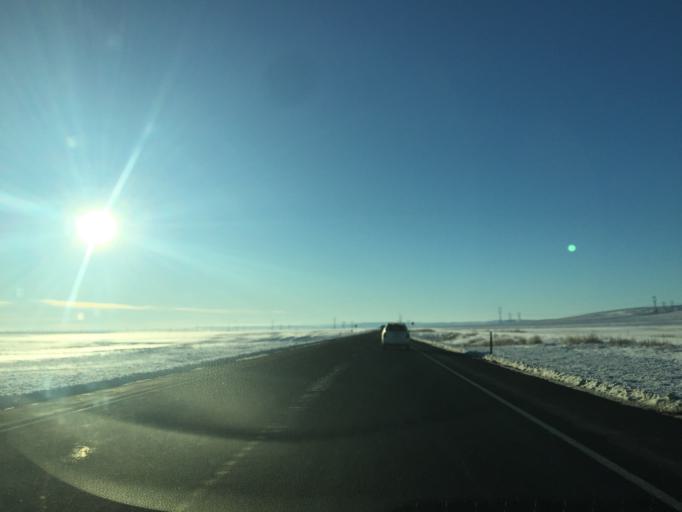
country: US
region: Washington
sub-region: Okanogan County
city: Coulee Dam
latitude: 47.6810
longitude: -119.1376
